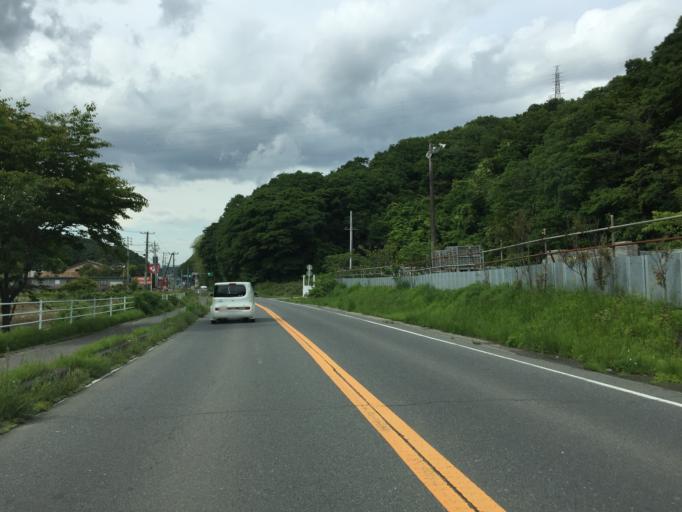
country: JP
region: Fukushima
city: Iwaki
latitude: 36.9632
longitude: 140.8718
